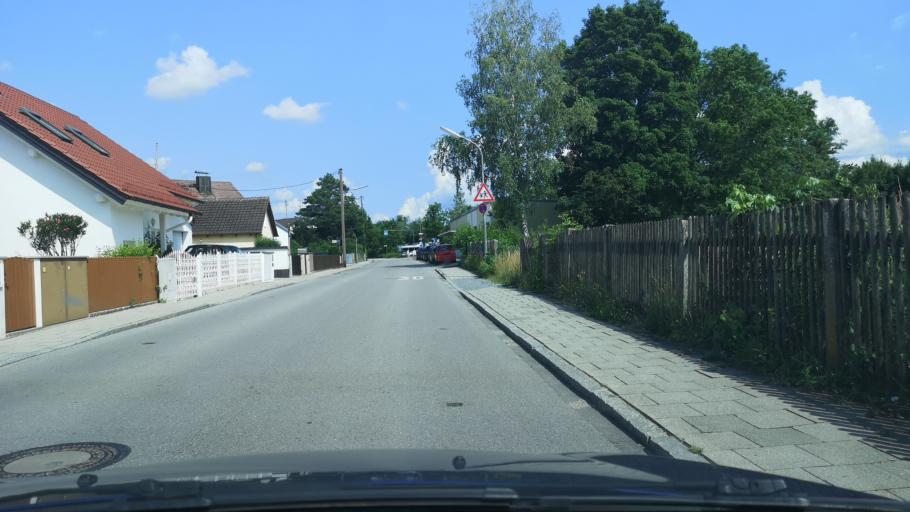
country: DE
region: Bavaria
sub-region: Upper Bavaria
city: Kirchheim bei Muenchen
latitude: 48.1593
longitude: 11.7581
